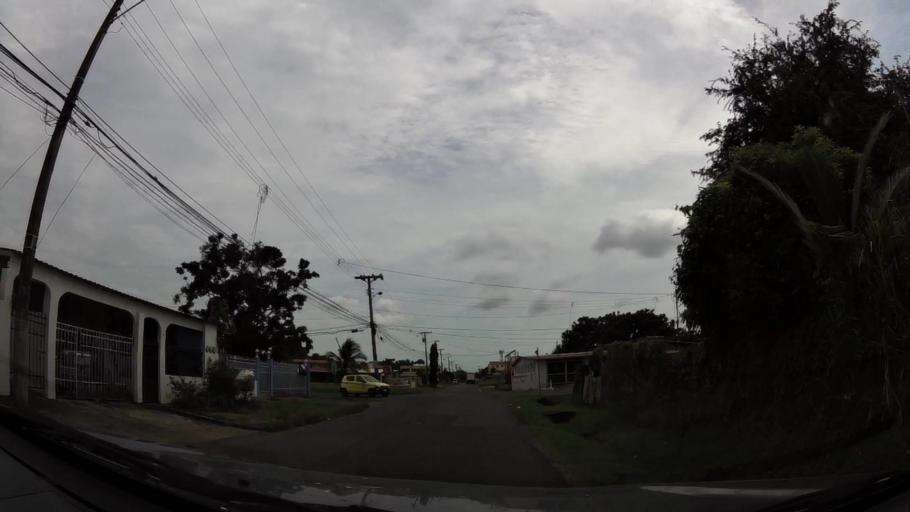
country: PA
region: Panama
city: San Miguelito
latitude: 9.0478
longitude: -79.4250
